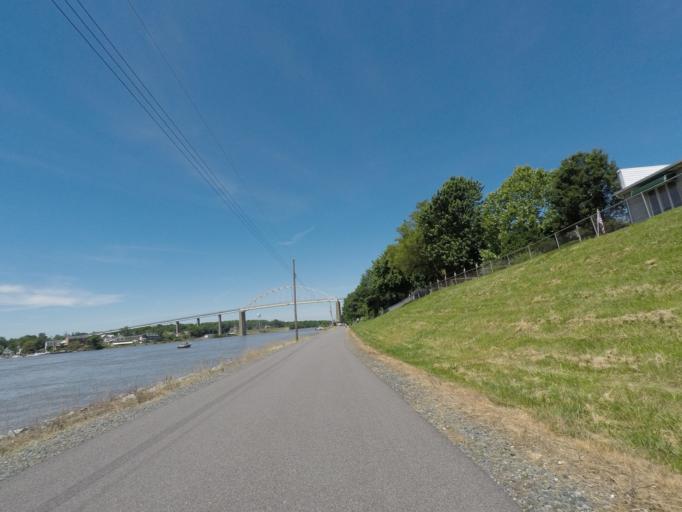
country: US
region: Maryland
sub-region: Cecil County
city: Elkton
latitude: 39.5295
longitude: -75.8073
